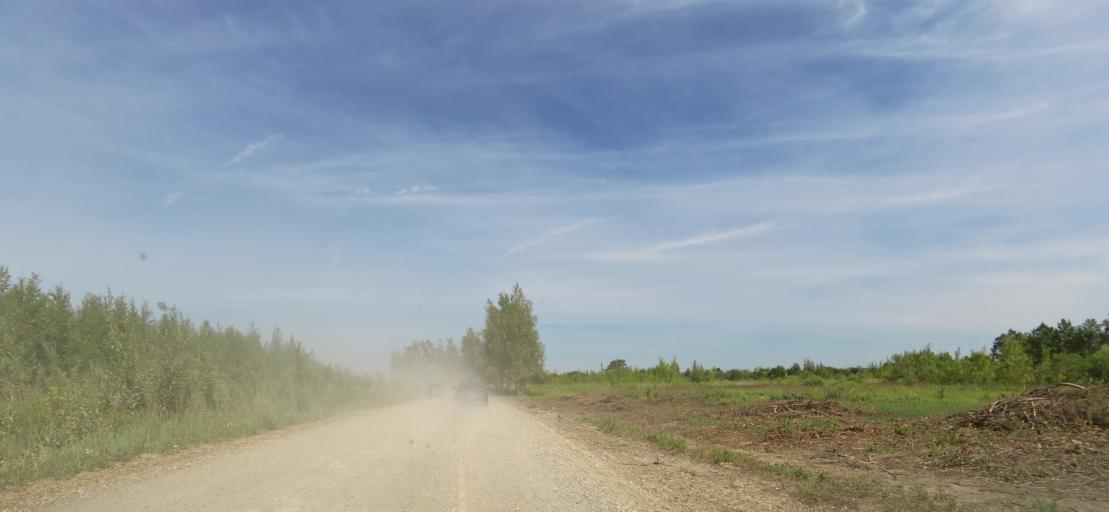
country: LT
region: Panevezys
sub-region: Panevezys City
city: Panevezys
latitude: 55.7228
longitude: 24.2947
